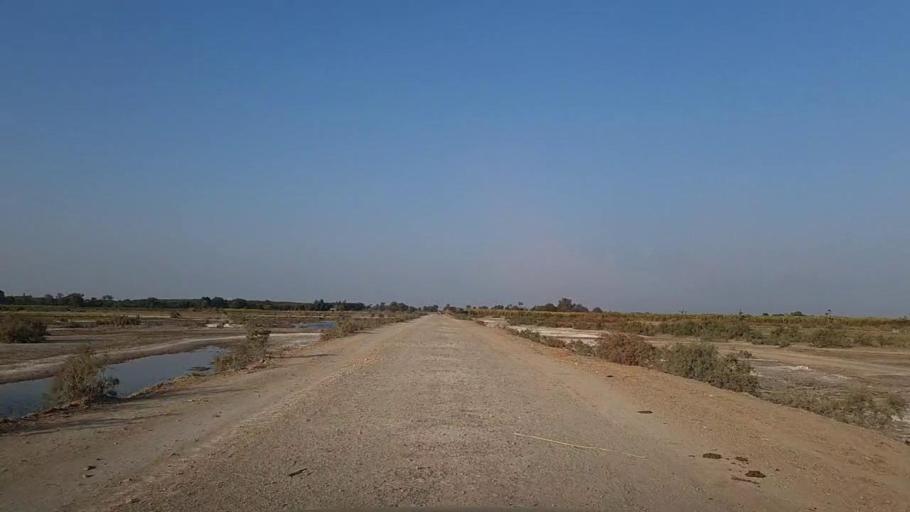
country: PK
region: Sindh
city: Tando Mittha Khan
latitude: 25.9354
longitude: 69.0701
